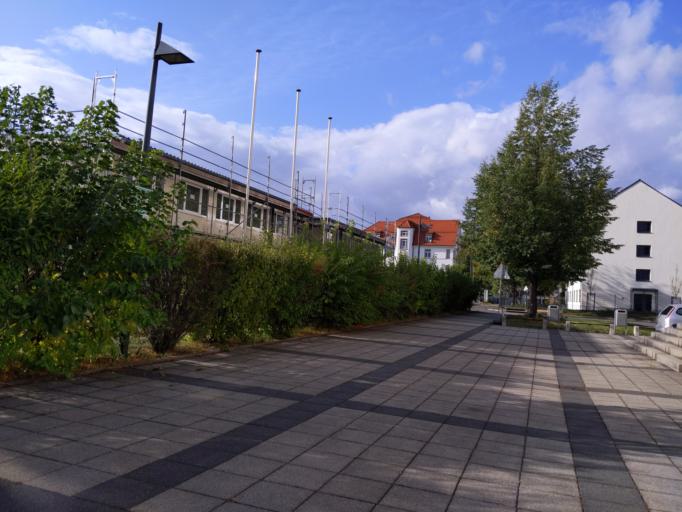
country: DE
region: Saxony
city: Meissen
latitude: 51.1592
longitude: 13.4893
